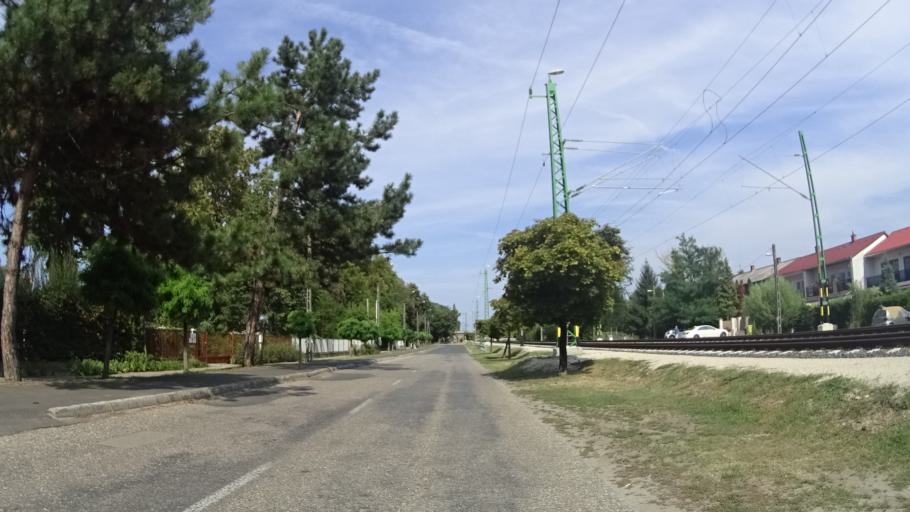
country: HU
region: Somogy
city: Balatonlelle
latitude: 46.7939
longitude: 17.7168
